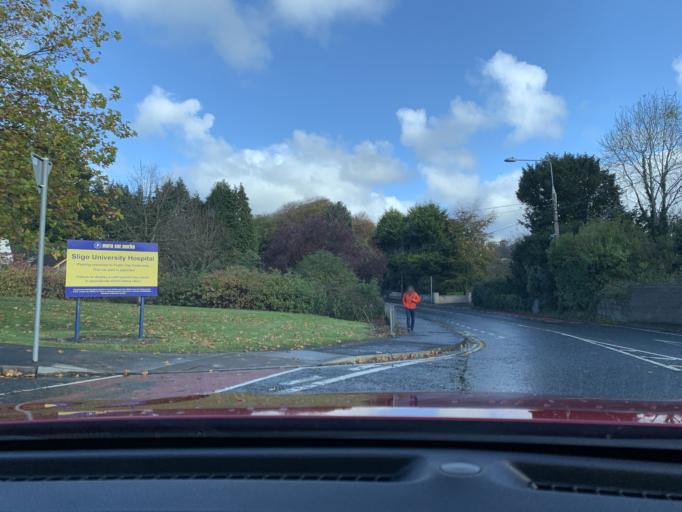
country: IE
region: Connaught
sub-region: Sligo
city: Sligo
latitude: 54.2739
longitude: -8.4617
